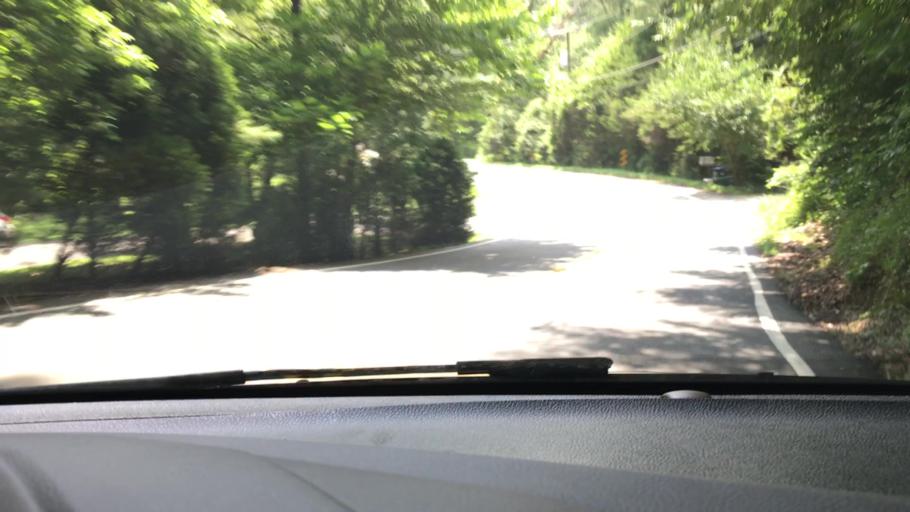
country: US
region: Maryland
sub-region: Montgomery County
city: Brookmont
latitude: 38.9369
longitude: -77.1389
